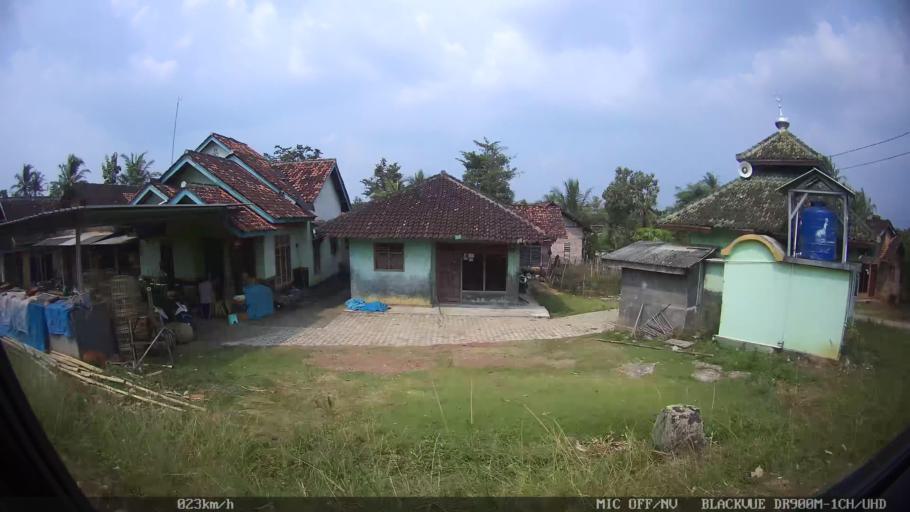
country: ID
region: Lampung
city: Gadingrejo
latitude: -5.3606
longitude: 105.0421
